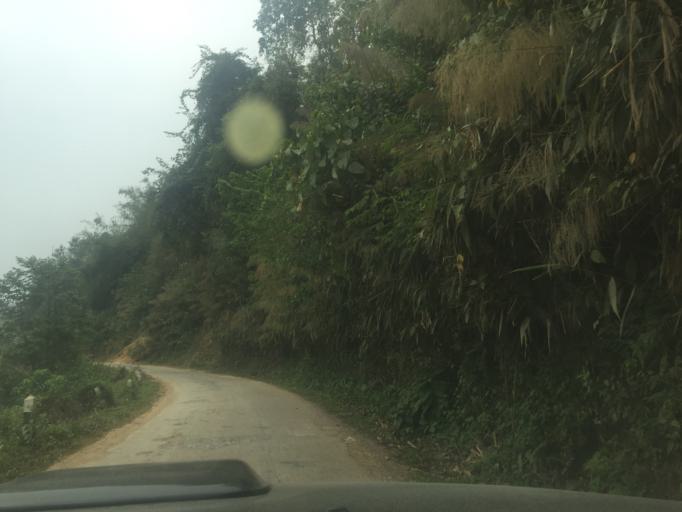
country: LA
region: Vientiane
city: Muang Sanakham
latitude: 18.3944
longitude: 101.5183
